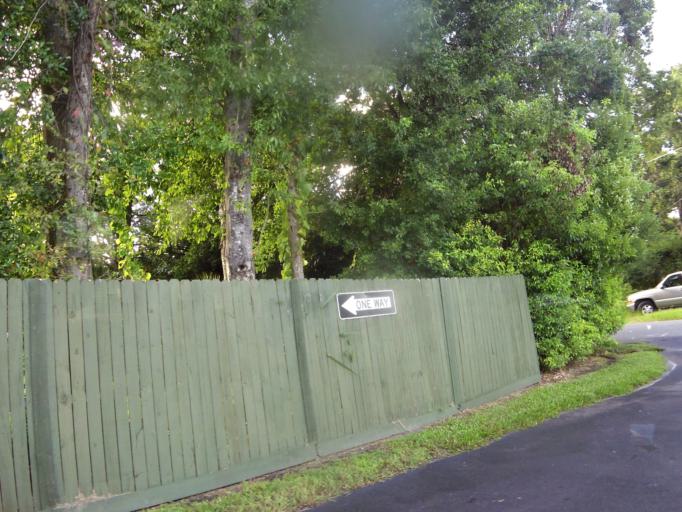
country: US
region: Florida
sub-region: Duval County
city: Jacksonville
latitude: 30.2884
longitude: -81.7254
